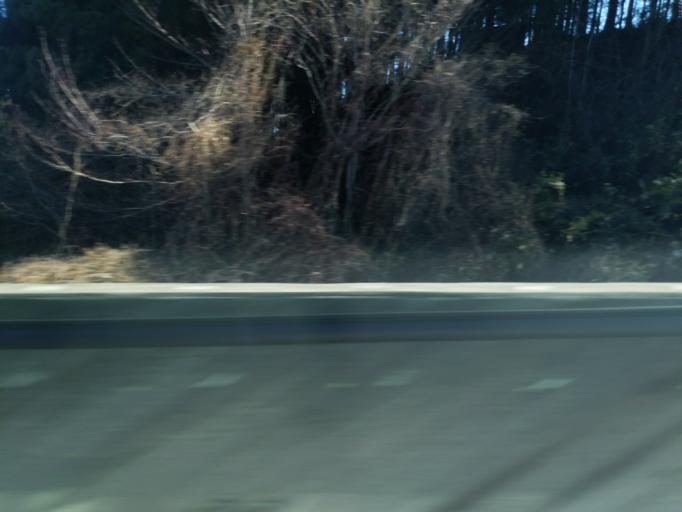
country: JP
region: Fukushima
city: Nihommatsu
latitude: 37.5545
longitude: 140.4529
